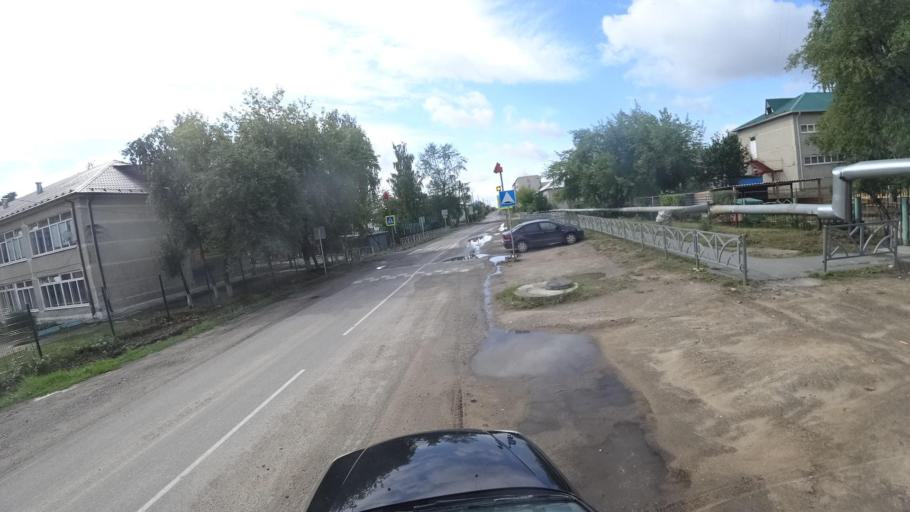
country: RU
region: Sverdlovsk
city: Kamyshlov
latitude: 56.8350
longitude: 62.7336
